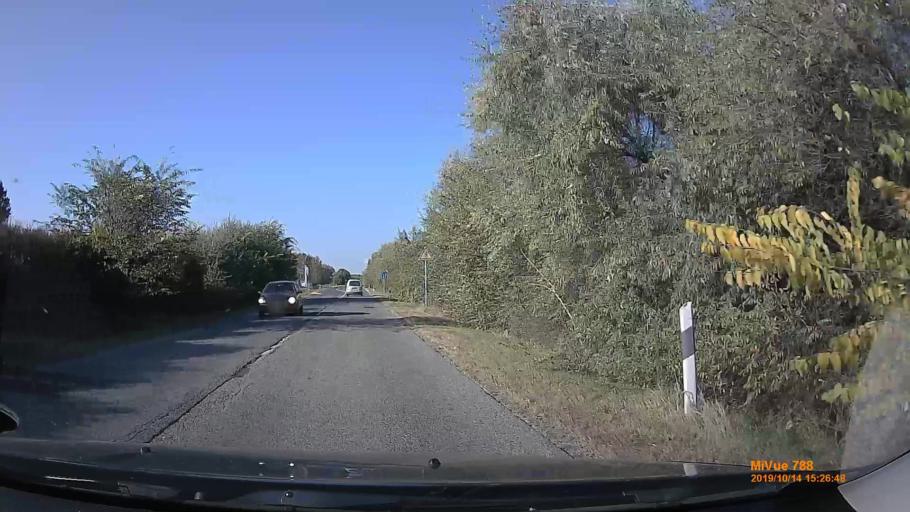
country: HU
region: Pest
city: Ecser
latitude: 47.4230
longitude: 19.3112
